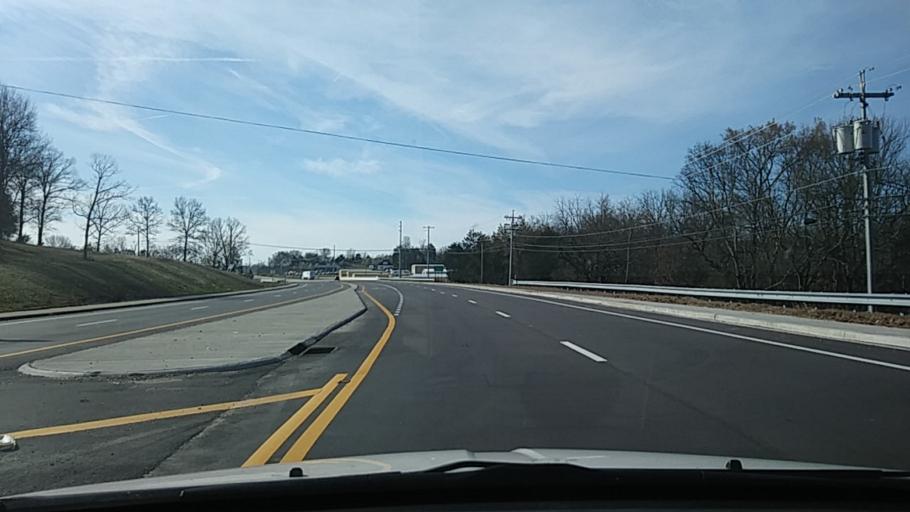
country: US
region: Tennessee
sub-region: Sumner County
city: Gallatin
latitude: 36.3484
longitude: -86.4390
